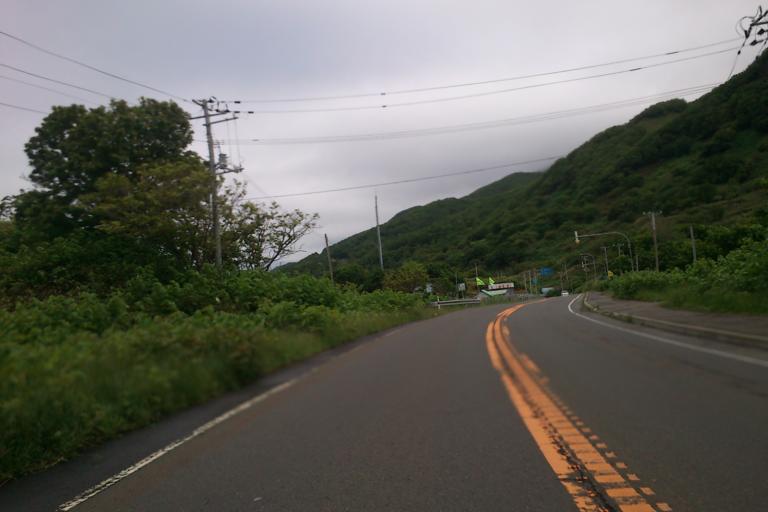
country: JP
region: Hokkaido
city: Ishikari
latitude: 43.4180
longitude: 141.4297
